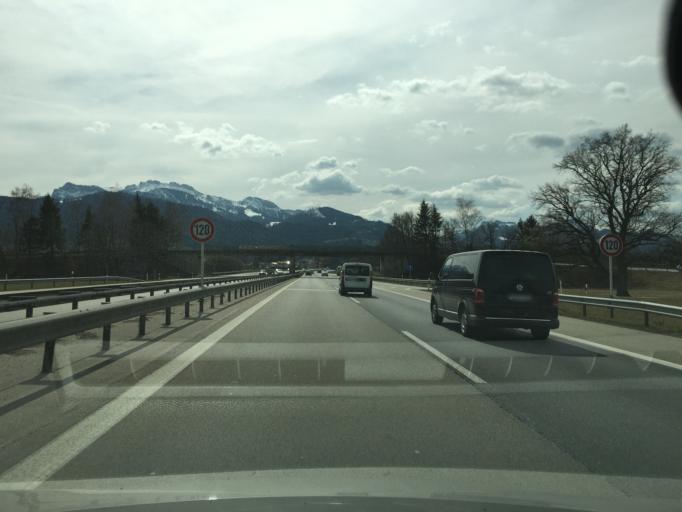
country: DE
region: Bavaria
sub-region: Upper Bavaria
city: Bernau am Chiemsee
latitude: 47.8281
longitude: 12.3850
